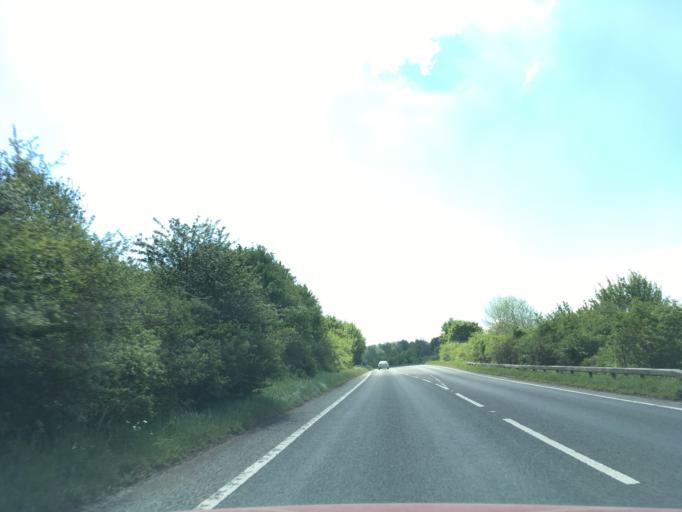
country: GB
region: England
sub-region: Northamptonshire
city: Brackley
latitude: 52.0261
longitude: -1.1586
